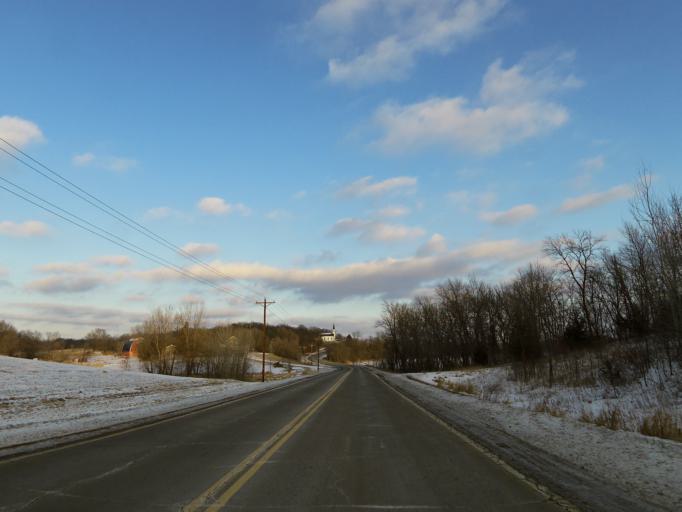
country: US
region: Minnesota
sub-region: Scott County
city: Prior Lake
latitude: 44.6305
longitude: -93.4371
